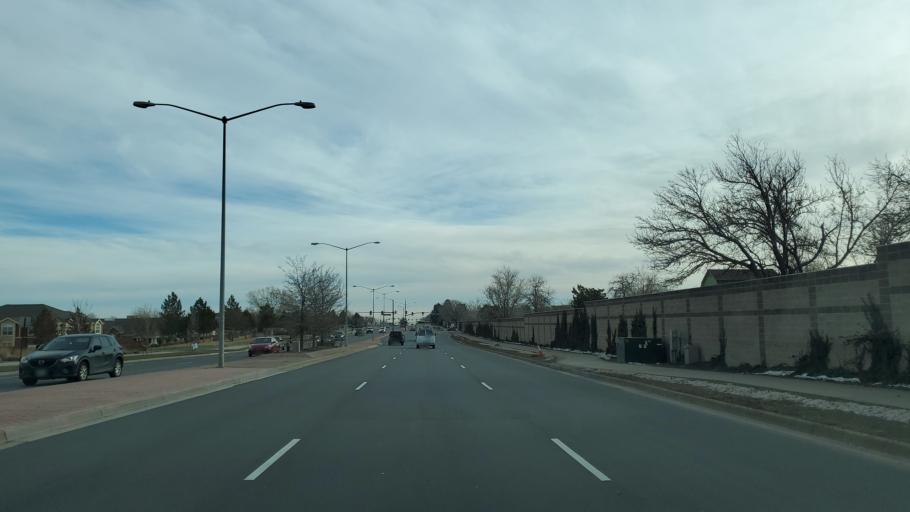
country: US
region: Colorado
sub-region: Adams County
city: Northglenn
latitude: 39.9138
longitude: -104.9485
